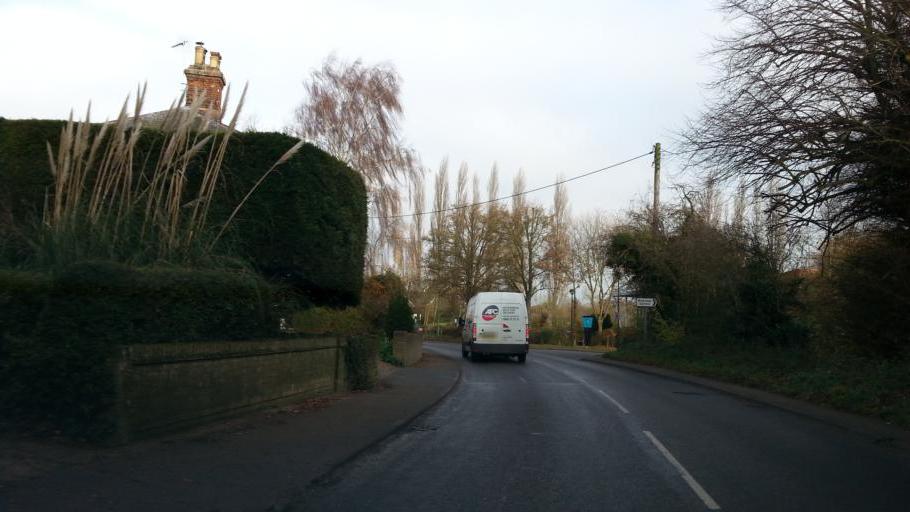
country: GB
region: England
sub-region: Suffolk
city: Framlingham
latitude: 52.2142
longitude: 1.3427
